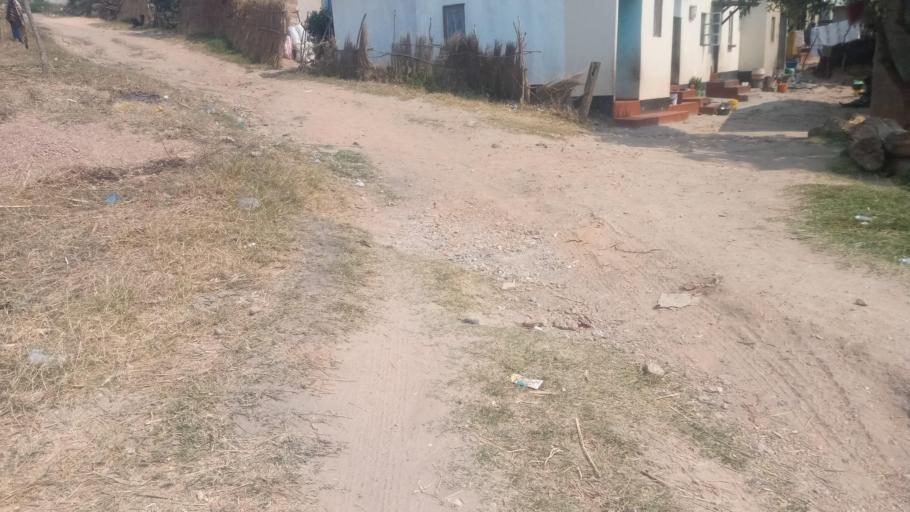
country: ZM
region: Lusaka
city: Lusaka
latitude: -15.4412
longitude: 28.3878
